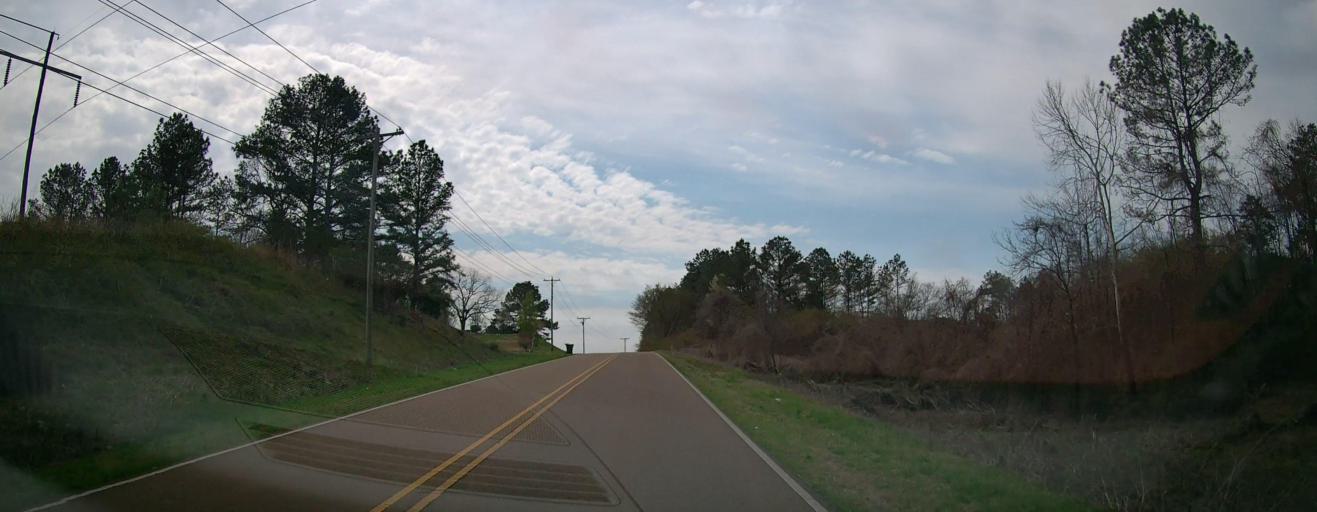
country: US
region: Mississippi
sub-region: Marshall County
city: Holly Springs
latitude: 34.7555
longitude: -89.4296
